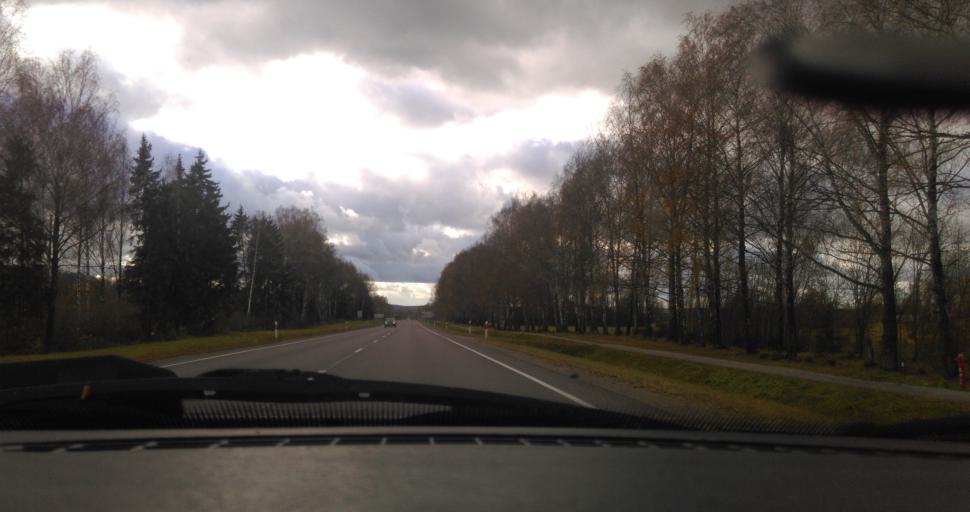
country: LT
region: Utenos apskritis
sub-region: Utena
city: Utena
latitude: 55.5103
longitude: 25.6372
